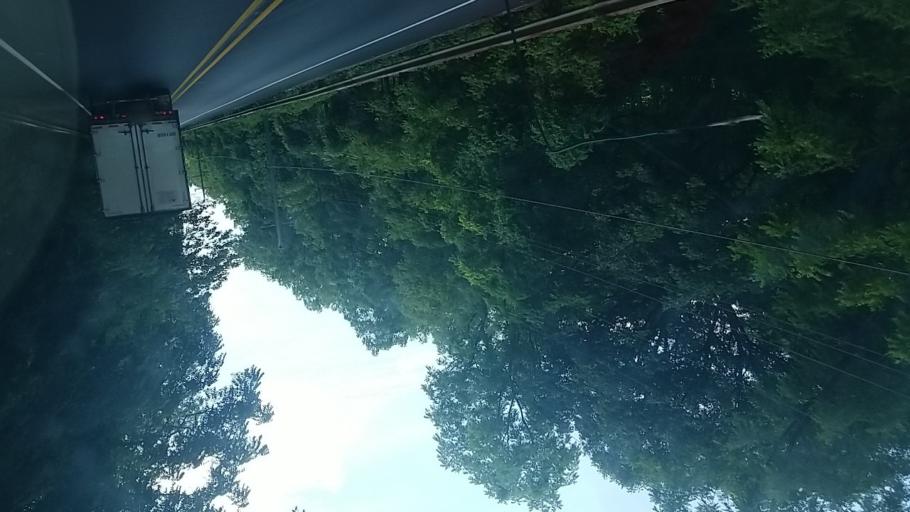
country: US
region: Pennsylvania
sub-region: Chester County
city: Toughkenamon
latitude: 39.8134
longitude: -75.7612
